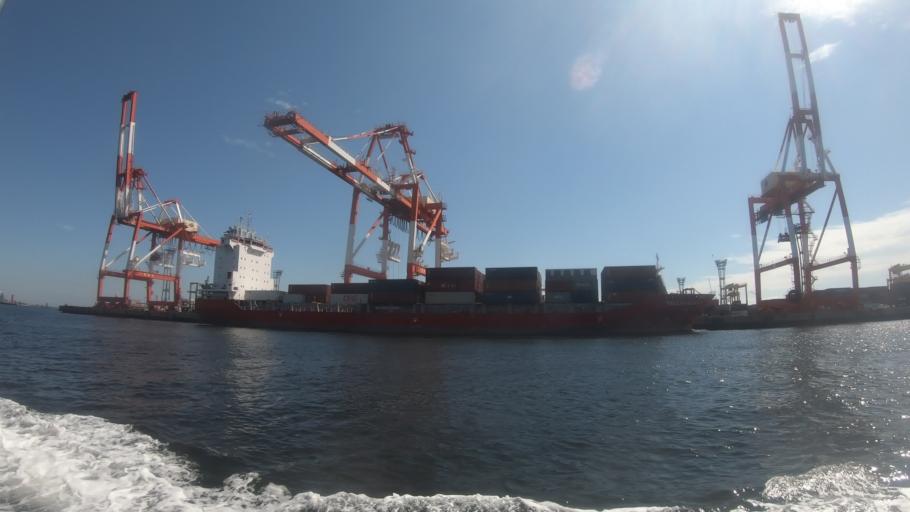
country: JP
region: Kanagawa
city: Yokohama
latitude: 35.4407
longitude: 139.6830
